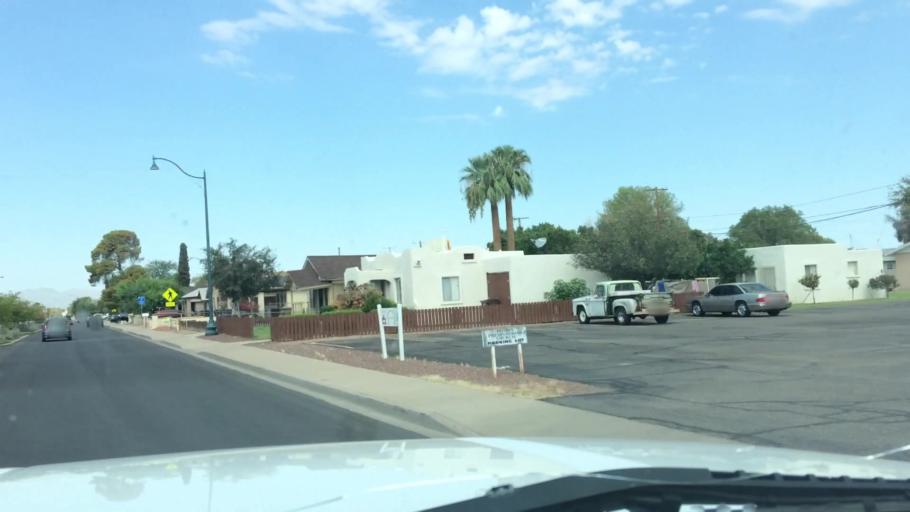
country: US
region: Arizona
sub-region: Maricopa County
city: Peoria
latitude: 33.5774
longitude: -112.2381
